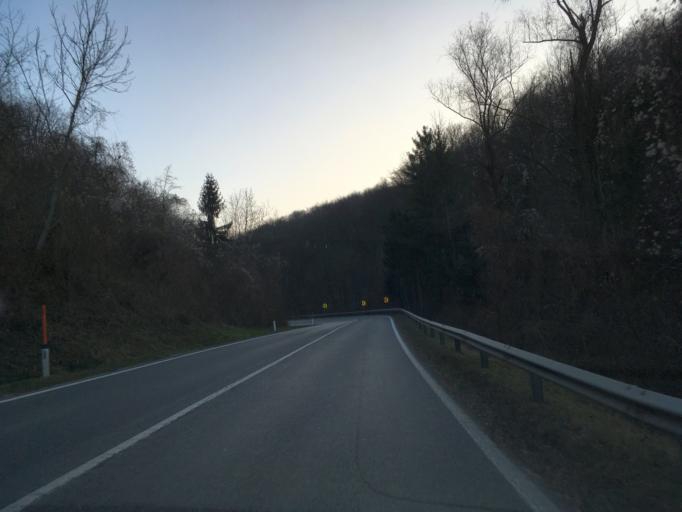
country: AT
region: Lower Austria
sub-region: Politischer Bezirk Tulln
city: Wordern
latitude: 48.3164
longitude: 16.2124
